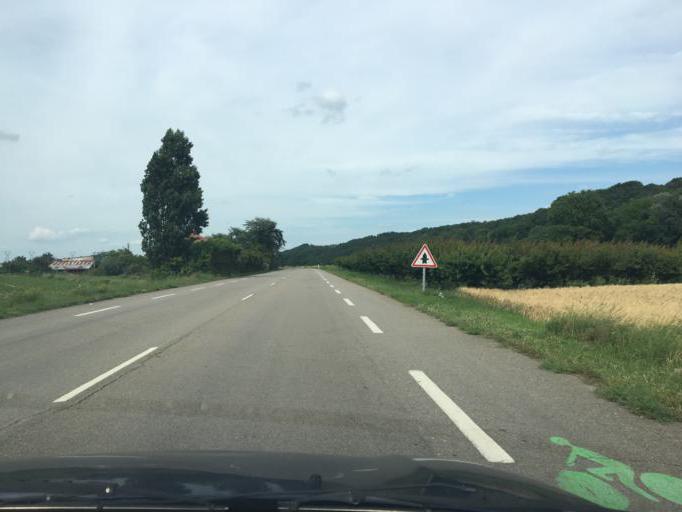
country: FR
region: Rhone-Alpes
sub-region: Departement de la Drome
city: Bourg-les-Valence
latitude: 44.9848
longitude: 4.9022
